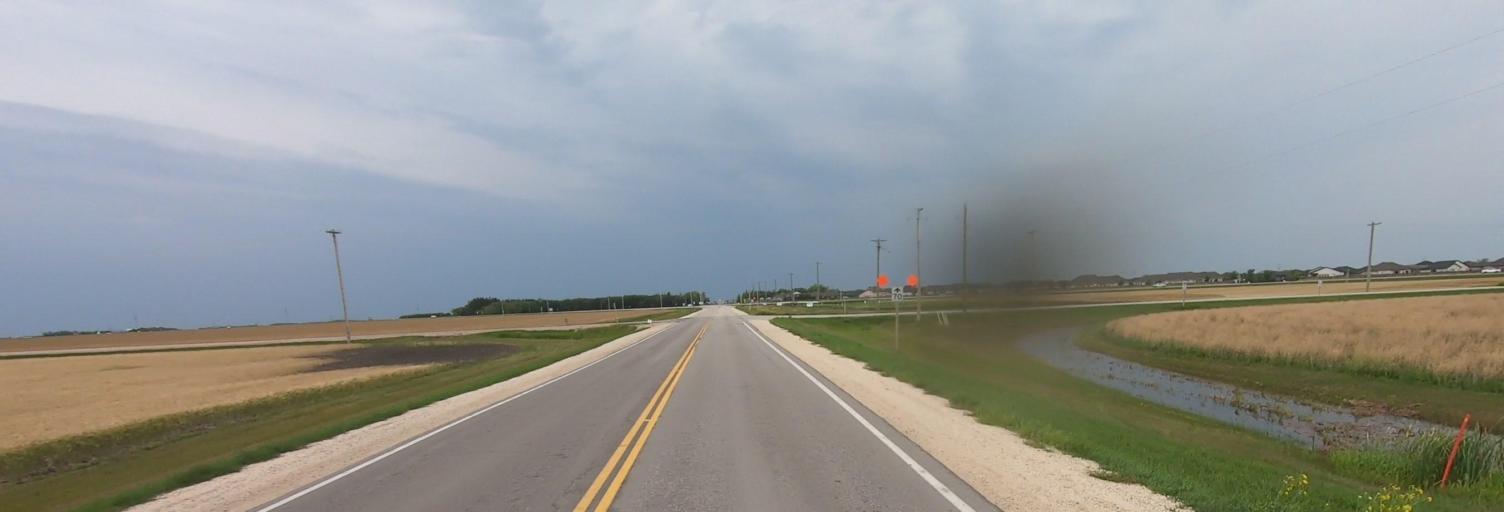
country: CA
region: Manitoba
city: Headingley
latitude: 49.7682
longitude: -97.3210
